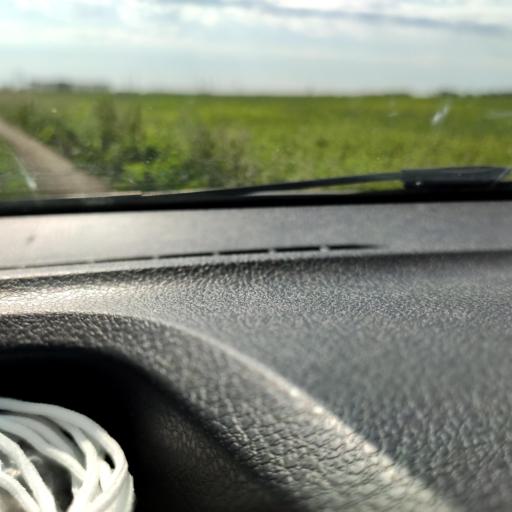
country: RU
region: Bashkortostan
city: Mikhaylovka
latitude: 54.8287
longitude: 55.7541
